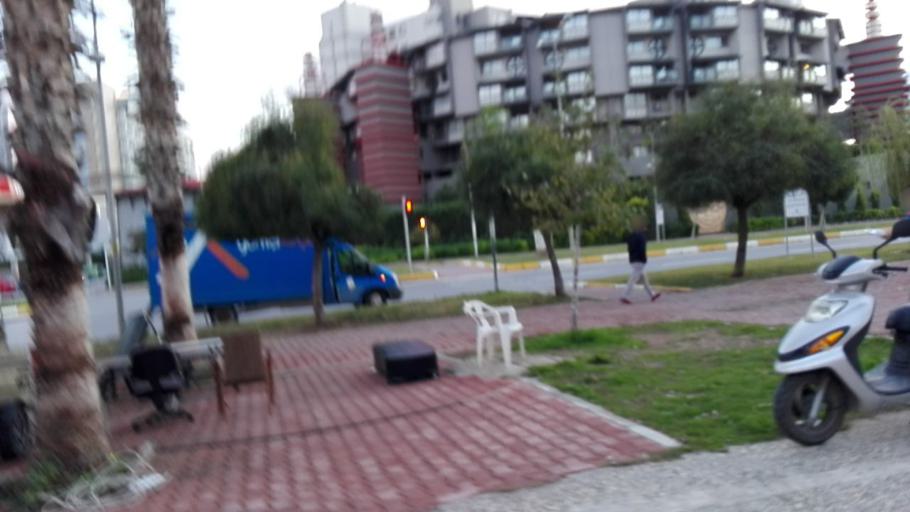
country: TR
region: Antalya
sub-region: Serik
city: Kumkoey
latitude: 36.8572
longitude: 30.8810
